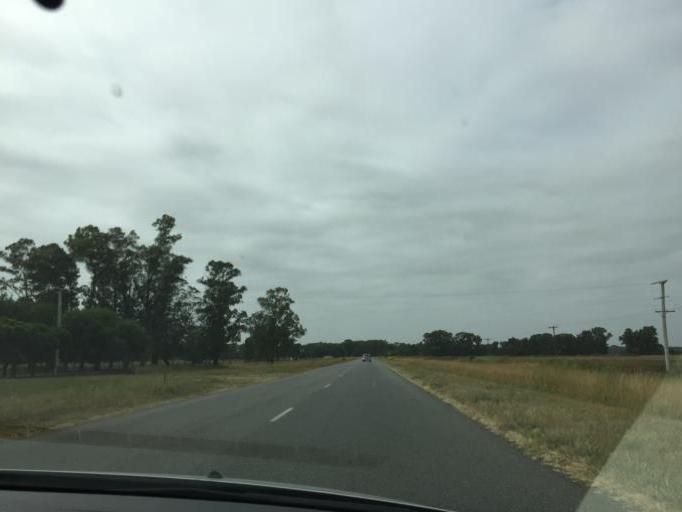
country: AR
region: Buenos Aires
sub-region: Partido de Las Flores
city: Las Flores
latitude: -36.2086
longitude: -59.0480
